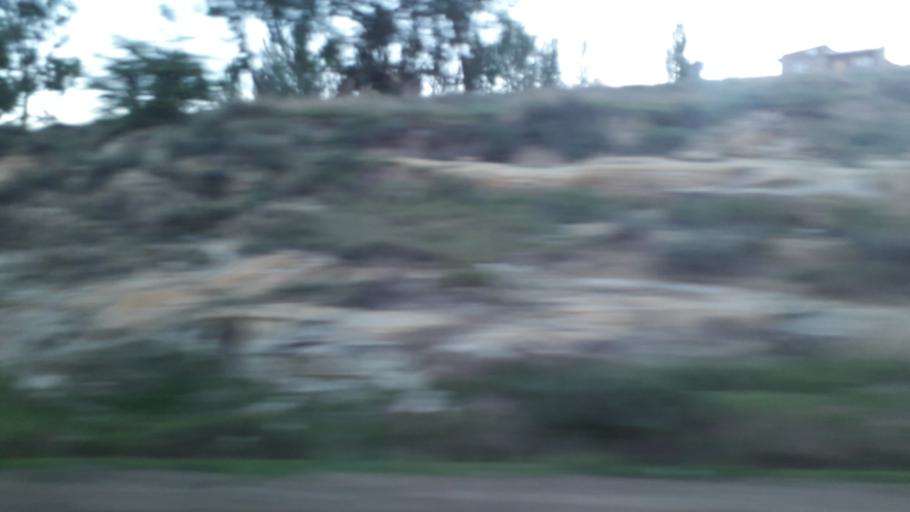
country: LS
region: Butha-Buthe
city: Butha-Buthe
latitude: -28.7285
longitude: 28.3905
